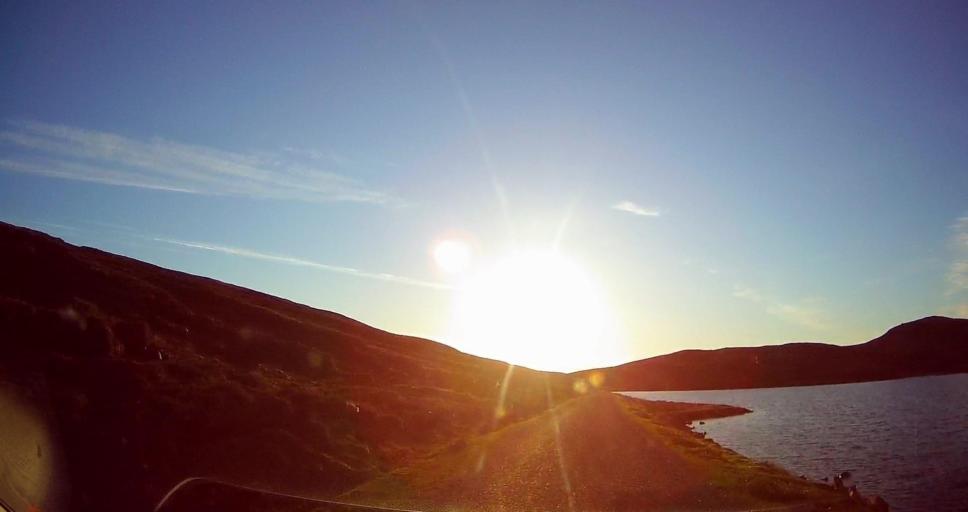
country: GB
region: Scotland
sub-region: Shetland Islands
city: Lerwick
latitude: 60.4431
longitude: -1.4068
